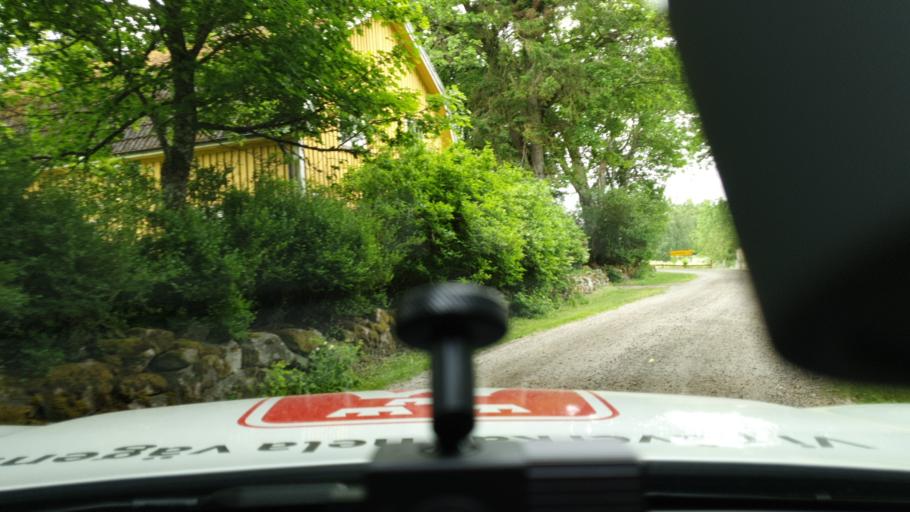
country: SE
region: Vaestra Goetaland
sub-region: Falkopings Kommun
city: Falkoeping
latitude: 58.0561
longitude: 13.6610
